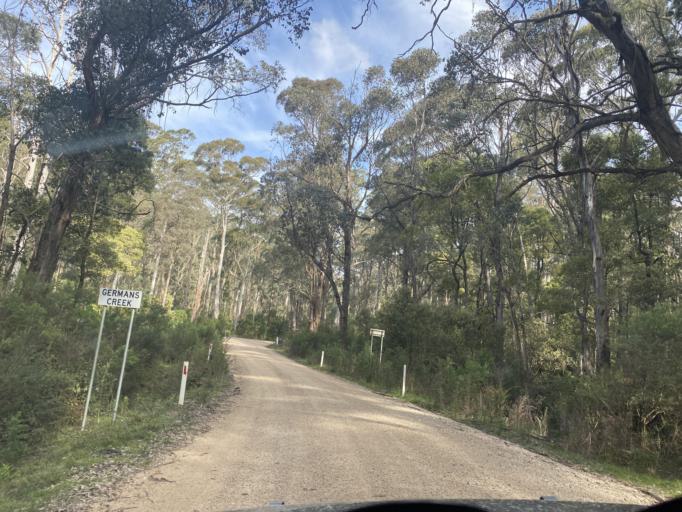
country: AU
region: Victoria
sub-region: Mansfield
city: Mansfield
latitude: -36.8647
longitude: 146.1980
